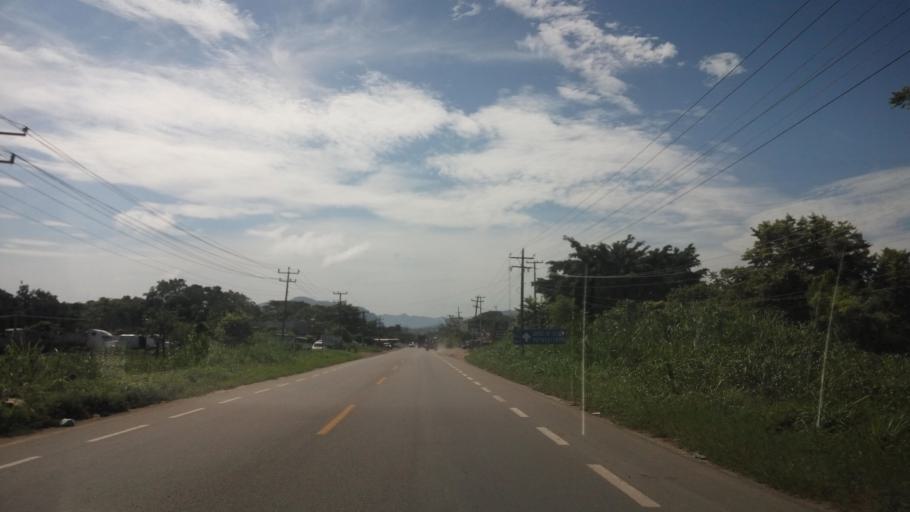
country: MX
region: Tabasco
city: Teapa
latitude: 17.5756
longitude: -92.9589
